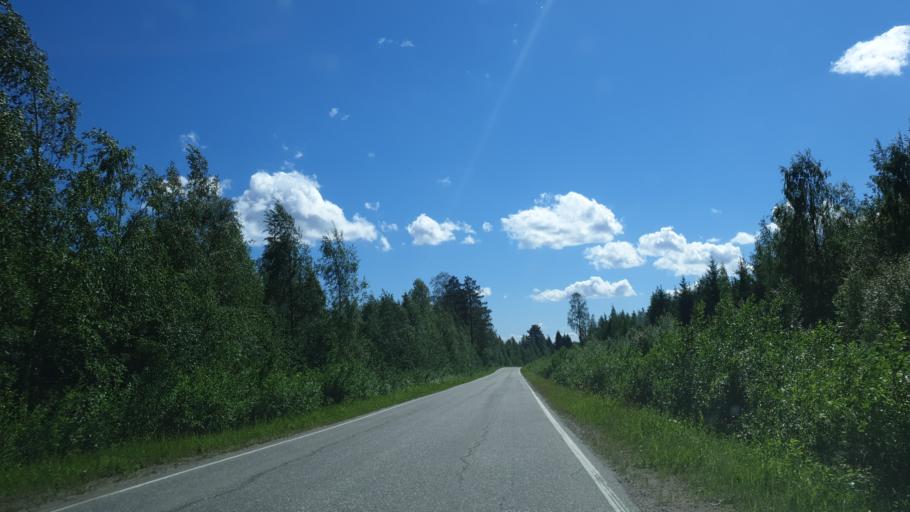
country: FI
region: Northern Savo
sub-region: Koillis-Savo
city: Kaavi
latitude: 62.9913
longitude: 28.5045
